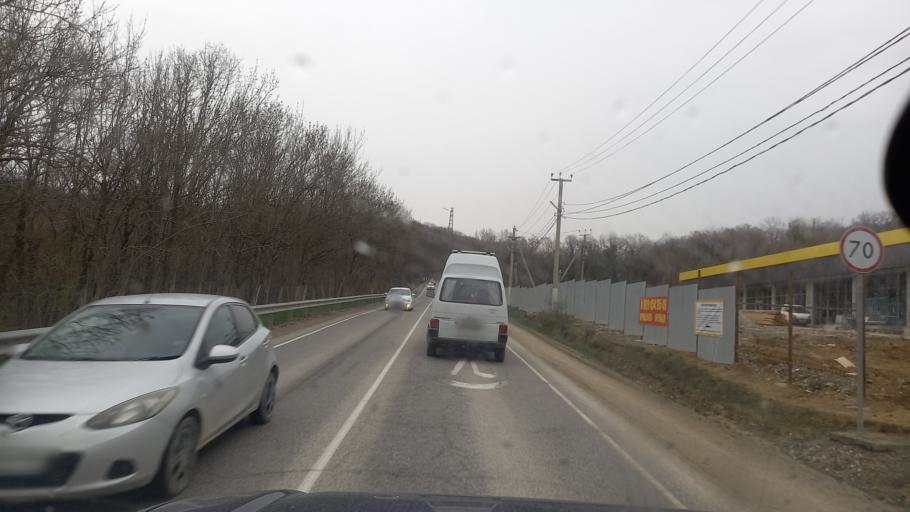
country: RU
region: Krasnodarskiy
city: Gayduk
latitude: 44.7374
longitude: 37.6771
